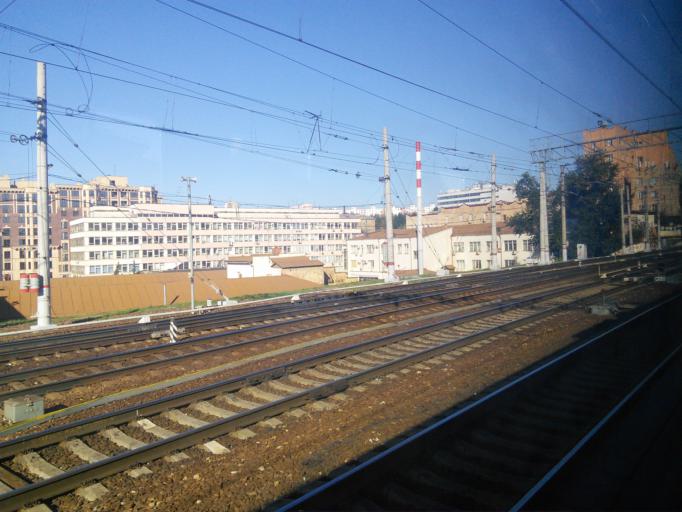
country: RU
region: Moscow
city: Taganskiy
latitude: 55.7522
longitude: 37.6674
